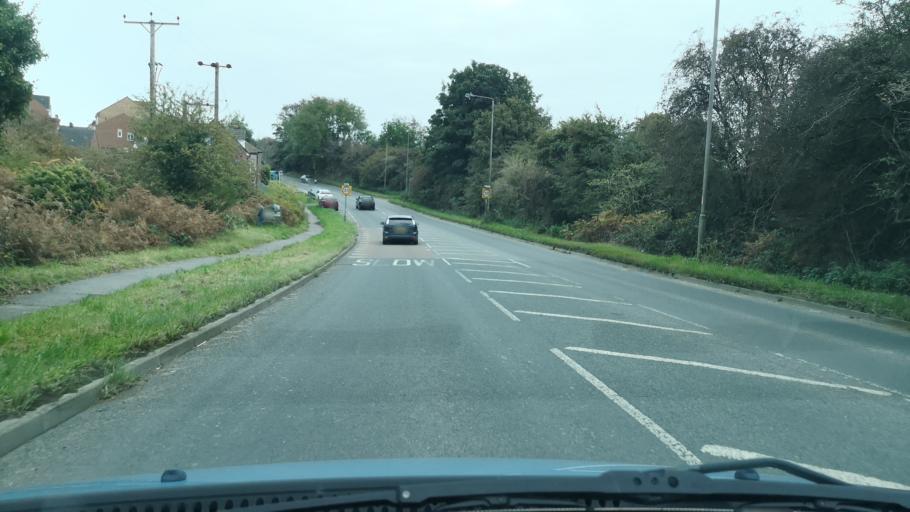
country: GB
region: England
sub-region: City and Borough of Wakefield
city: Fitzwilliam
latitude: 53.6434
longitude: -1.3593
